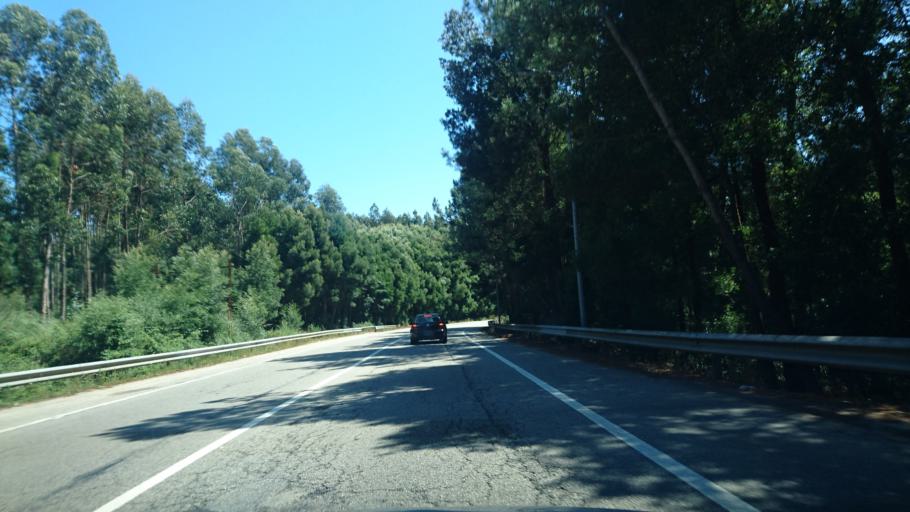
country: PT
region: Aveiro
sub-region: Espinho
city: Souto
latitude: 40.9698
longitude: -8.6110
